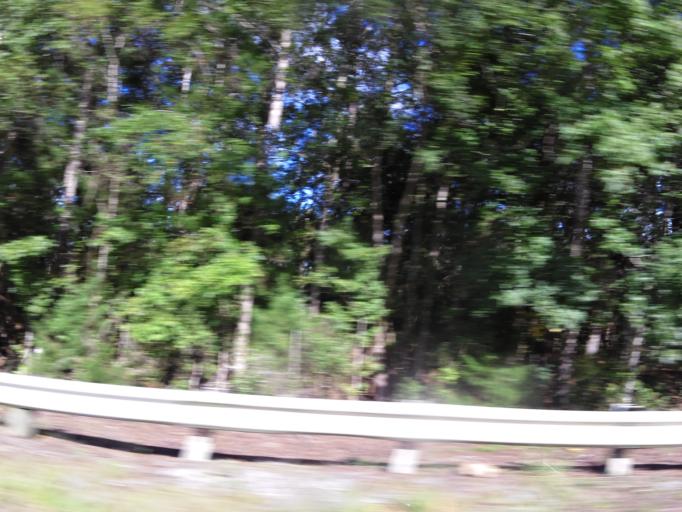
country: US
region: Georgia
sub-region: Camden County
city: Woodbine
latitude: 31.0823
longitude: -81.7265
